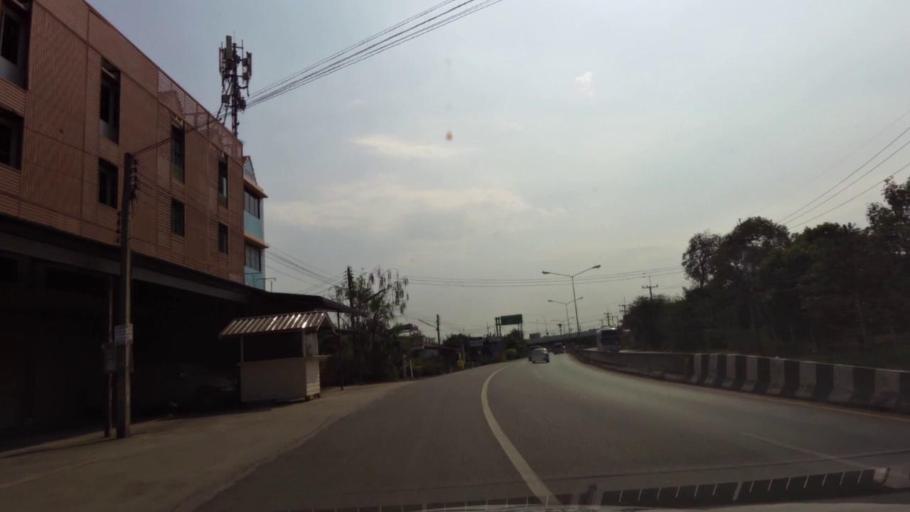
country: TH
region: Phra Nakhon Si Ayutthaya
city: Phra Nakhon Si Ayutthaya
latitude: 14.3322
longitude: 100.5783
